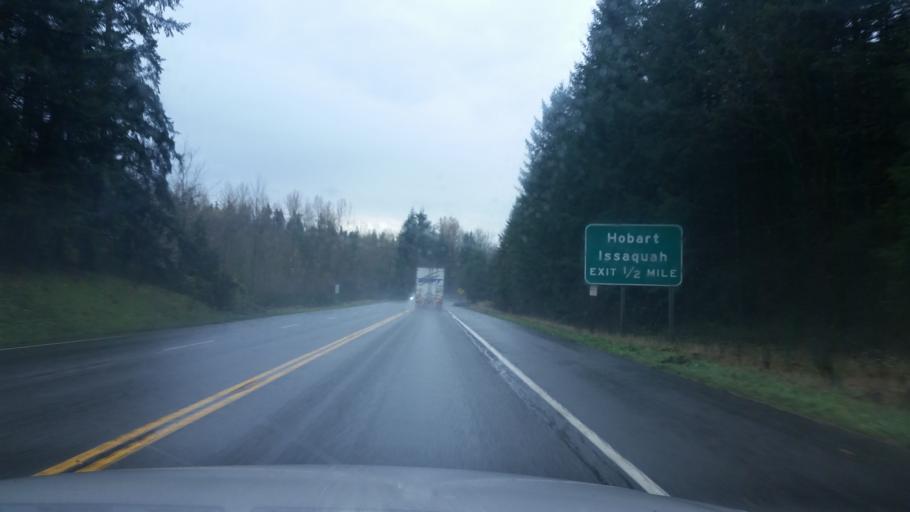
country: US
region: Washington
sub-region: King County
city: Hobart
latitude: 47.4423
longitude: -121.9623
